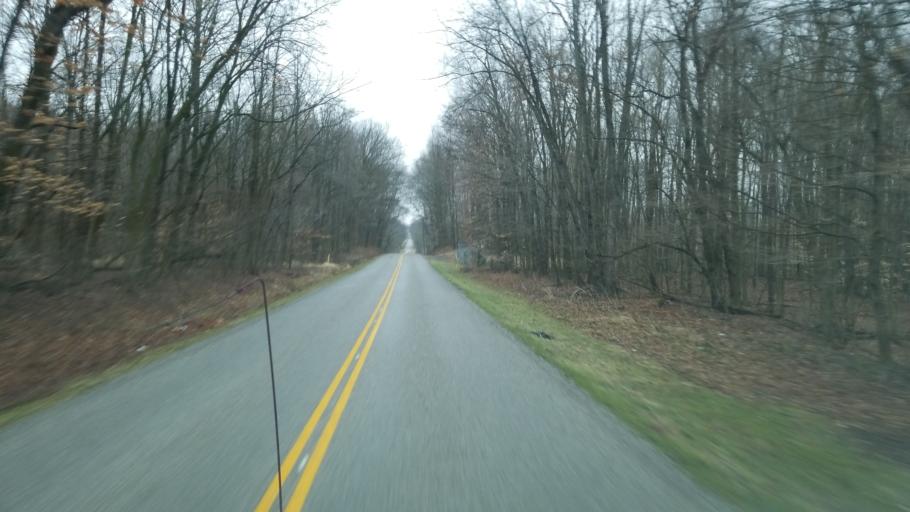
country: US
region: Ohio
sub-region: Wayne County
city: Orrville
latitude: 40.8863
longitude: -81.7834
